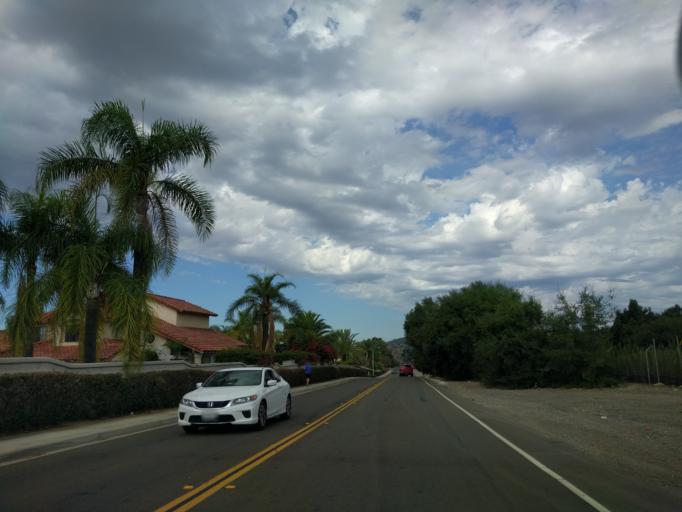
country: US
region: California
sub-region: Orange County
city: Trabuco Canyon
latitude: 33.6573
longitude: -117.5789
